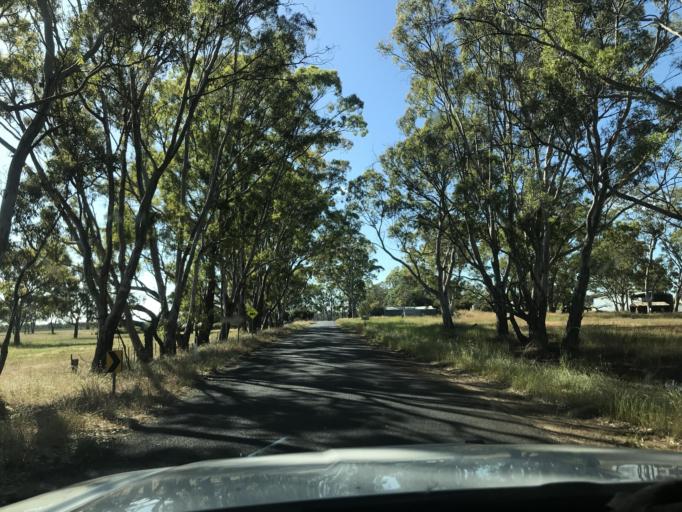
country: AU
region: Victoria
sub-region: Horsham
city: Horsham
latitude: -37.0316
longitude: 141.7274
